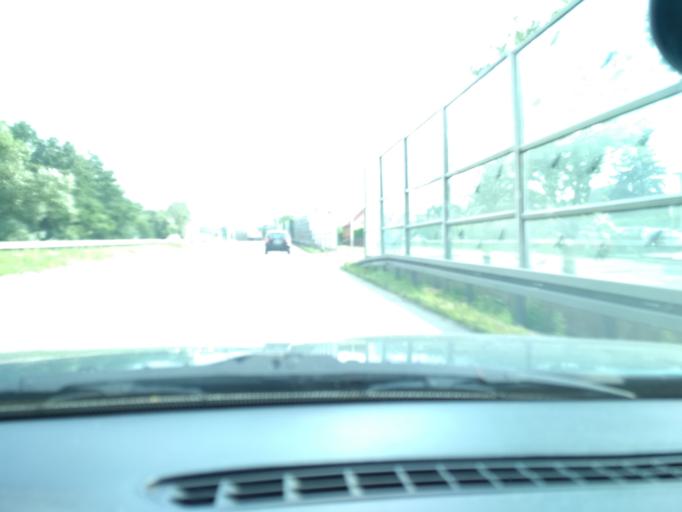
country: PL
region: Silesian Voivodeship
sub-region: Zory
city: Zory
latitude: 50.0180
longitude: 18.7074
